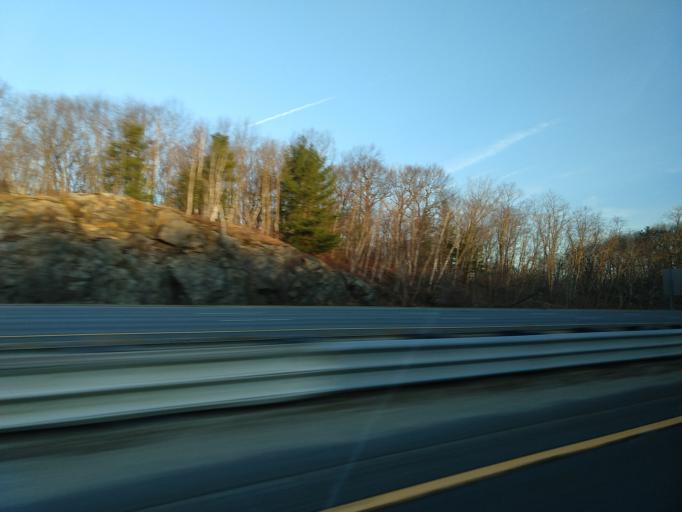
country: US
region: Massachusetts
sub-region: Essex County
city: South Peabody
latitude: 42.5372
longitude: -70.9841
